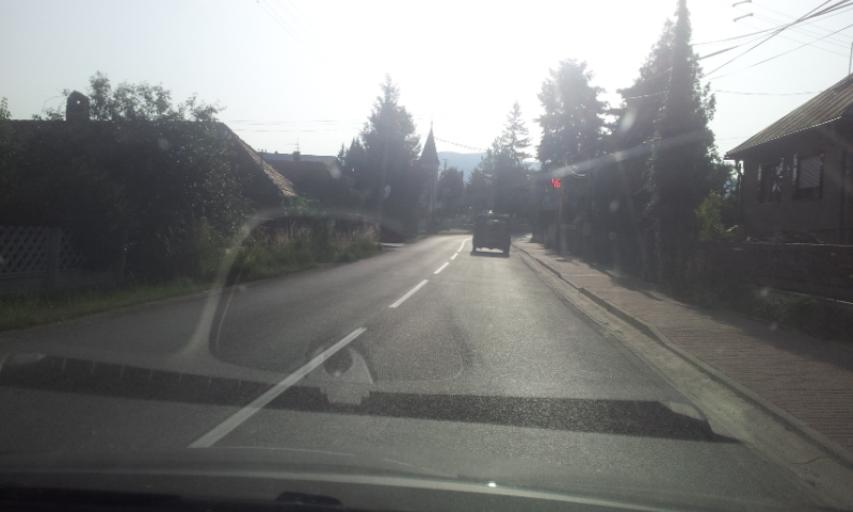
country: SK
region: Kosicky
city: Kosice
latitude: 48.6044
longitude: 21.3478
